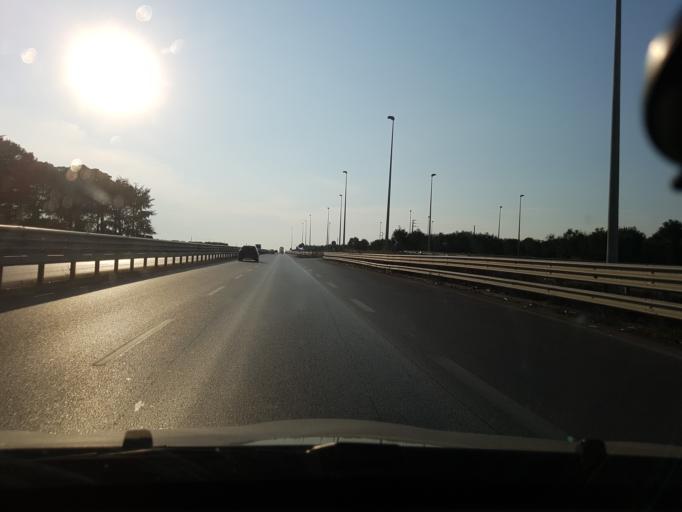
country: IT
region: Apulia
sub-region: Provincia di Foggia
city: Cerignola
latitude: 41.2788
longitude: 15.8604
